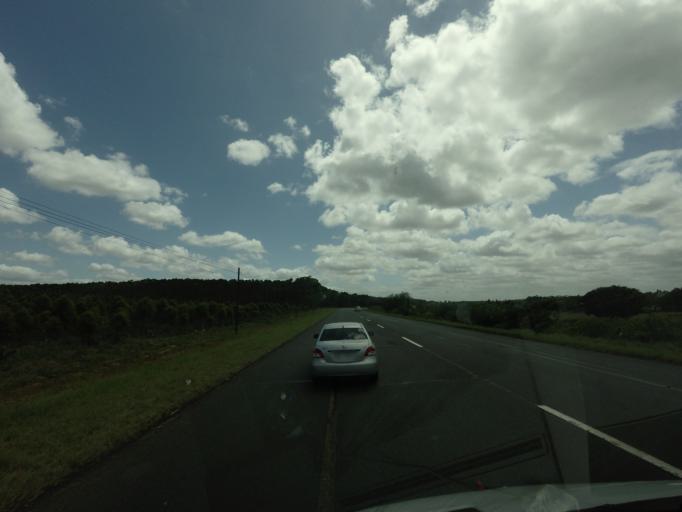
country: ZA
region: KwaZulu-Natal
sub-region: uThungulu District Municipality
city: KwaMbonambi
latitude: -28.5514
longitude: 32.1189
